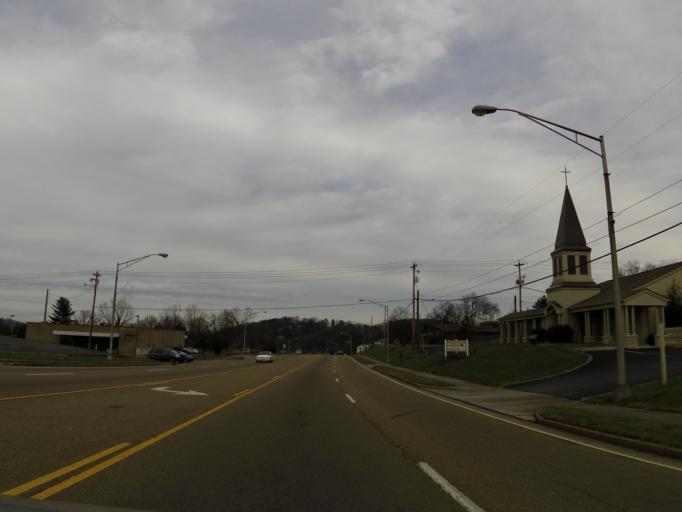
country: US
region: Tennessee
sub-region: Cocke County
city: Newport
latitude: 35.9634
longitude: -83.1944
